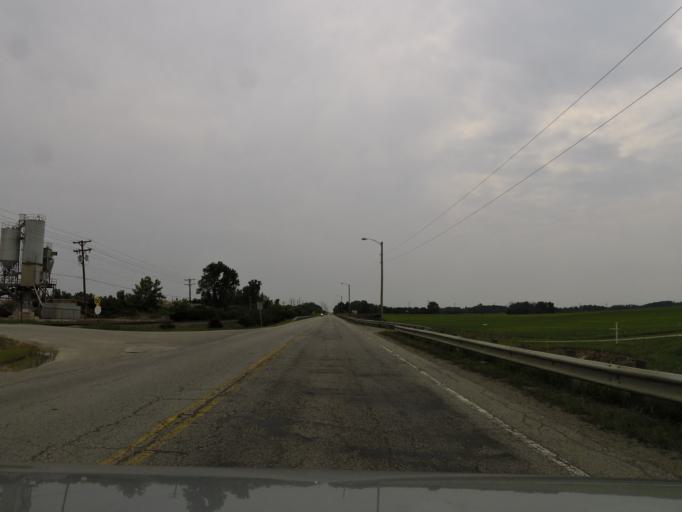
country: US
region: Ohio
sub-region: Clinton County
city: Wilmington
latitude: 39.4262
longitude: -83.8348
